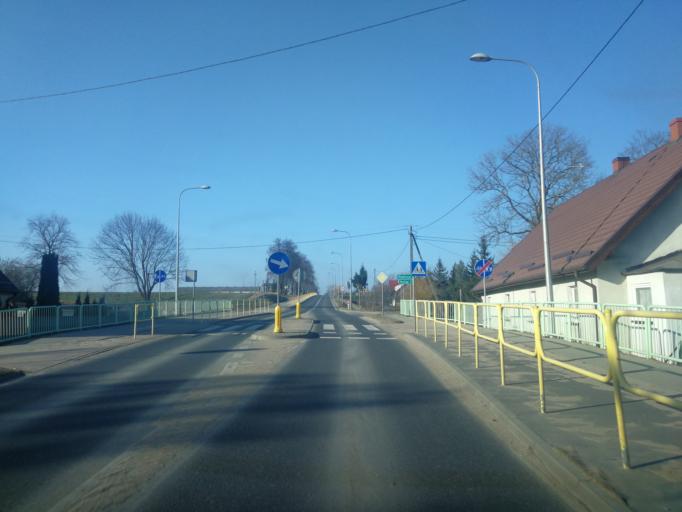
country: PL
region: Warmian-Masurian Voivodeship
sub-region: Powiat ilawski
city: Lubawa
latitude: 53.4563
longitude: 19.7785
